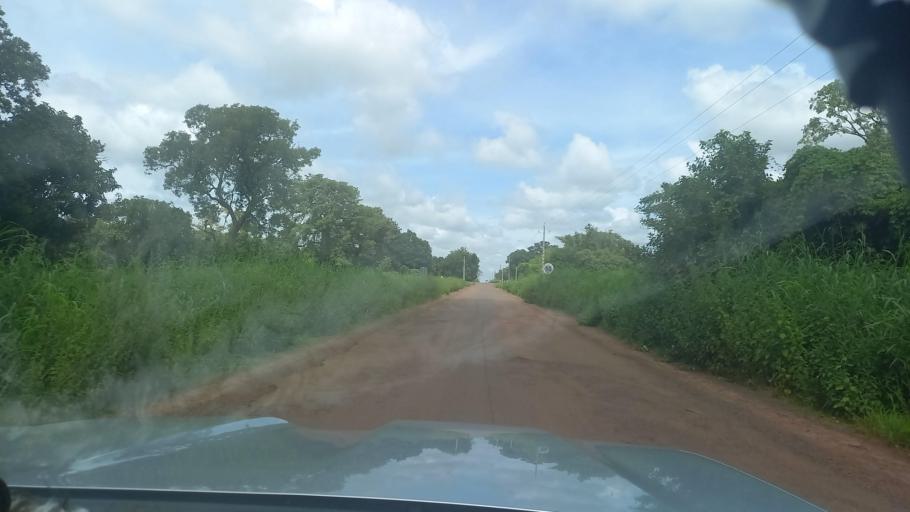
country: GM
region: Lower River
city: Kaiaf
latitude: 13.2187
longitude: -15.5424
